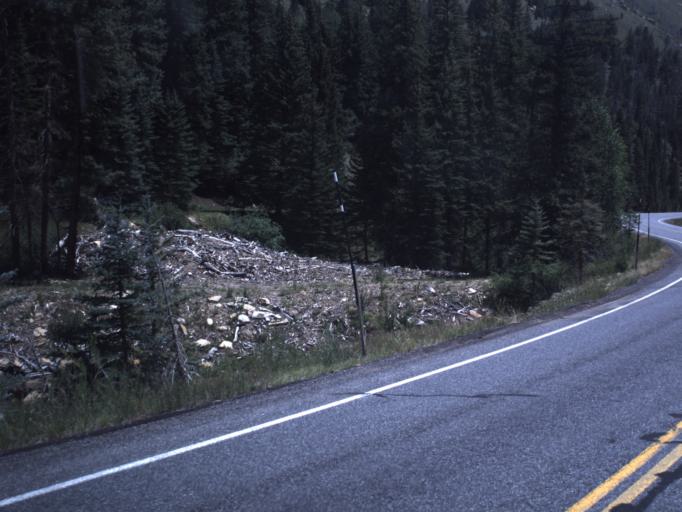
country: US
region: Utah
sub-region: Emery County
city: Huntington
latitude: 39.5009
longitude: -111.1592
